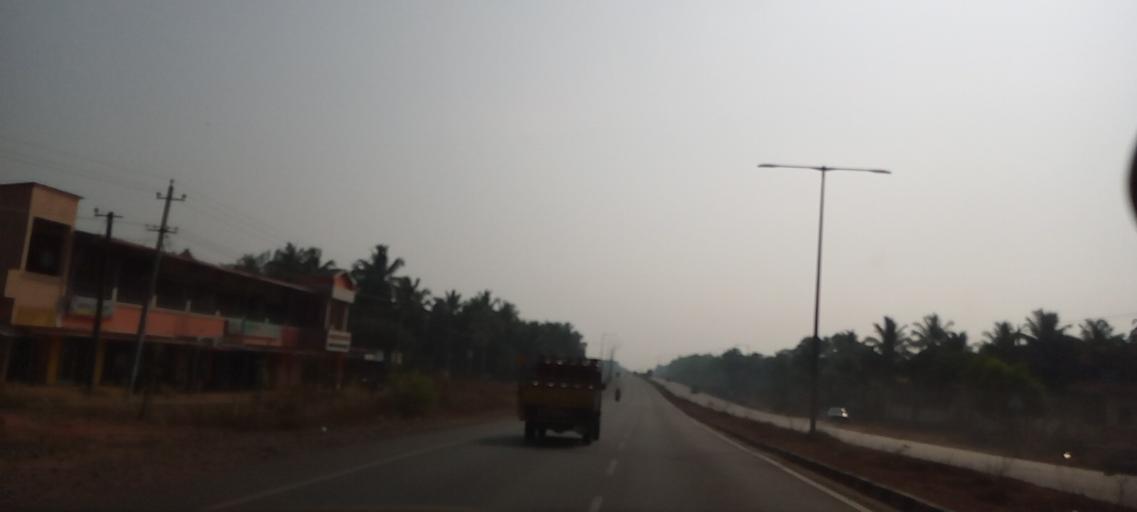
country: IN
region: Karnataka
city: Gangolli
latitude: 13.6879
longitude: 74.6567
